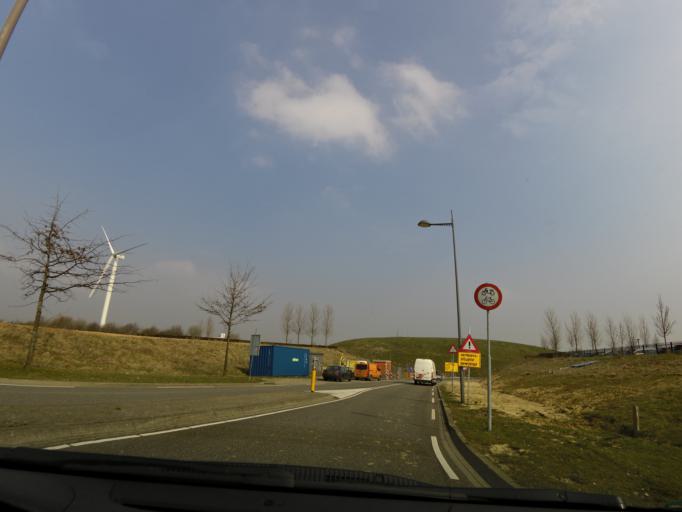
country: NL
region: Limburg
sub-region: Gemeente Simpelveld
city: Simpelveld
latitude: 50.8418
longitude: 6.0121
